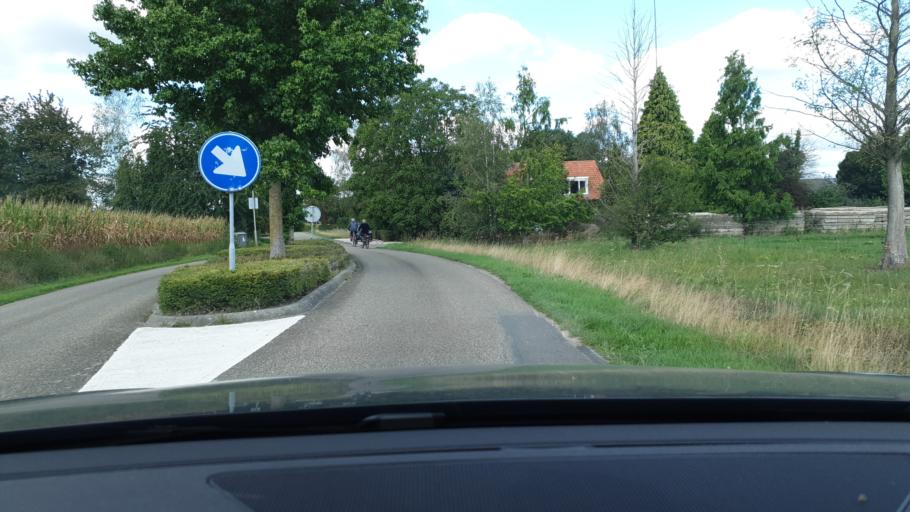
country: NL
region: Gelderland
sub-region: Gemeente Groesbeek
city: Bredeweg
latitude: 51.7539
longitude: 5.9506
